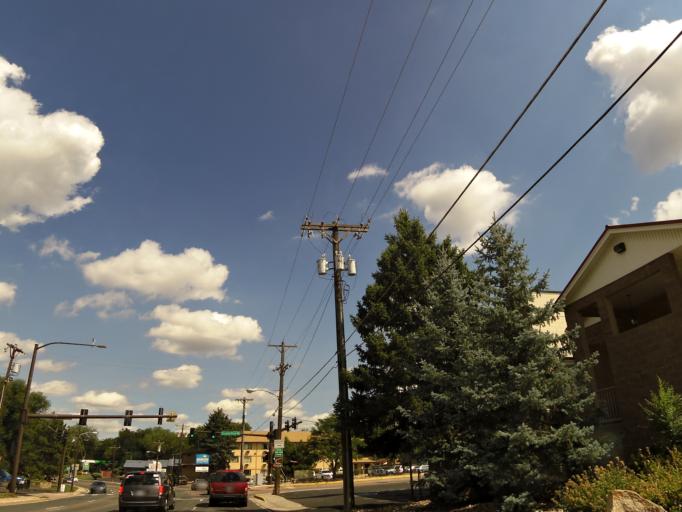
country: US
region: Colorado
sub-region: El Paso County
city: Manitou Springs
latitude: 38.8567
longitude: -104.8994
